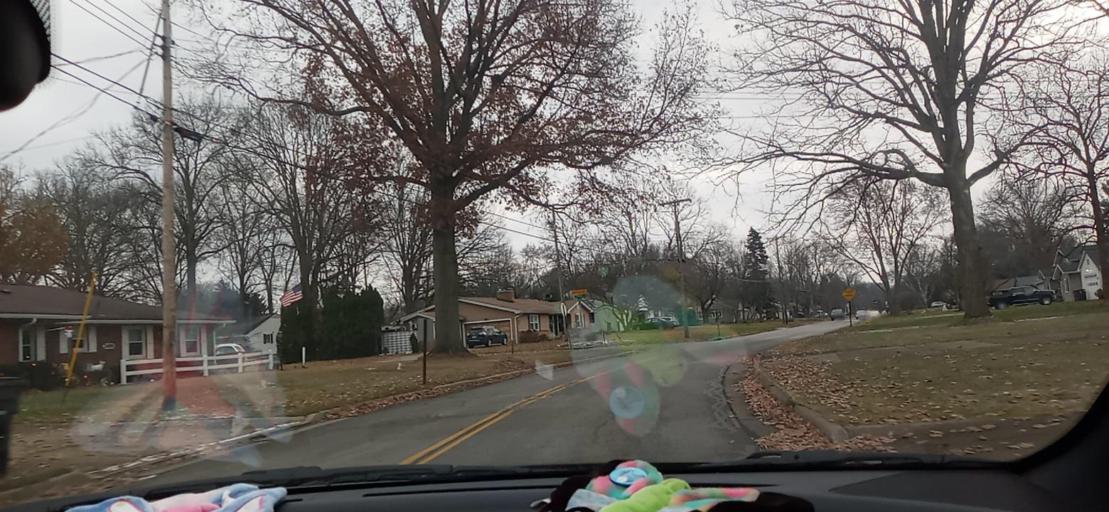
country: US
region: Ohio
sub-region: Summit County
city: Fairlawn
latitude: 41.1290
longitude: -81.5821
